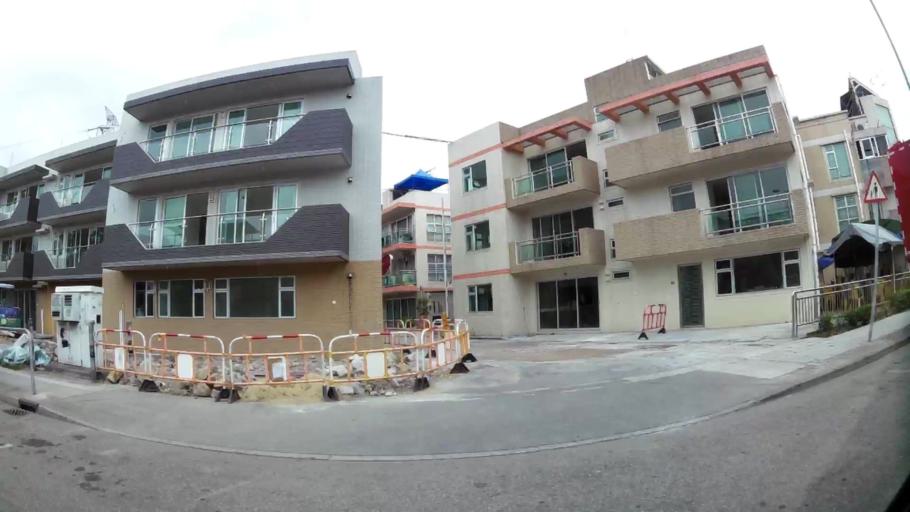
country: HK
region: Tuen Mun
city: Tuen Mun
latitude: 22.4246
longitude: 113.9912
